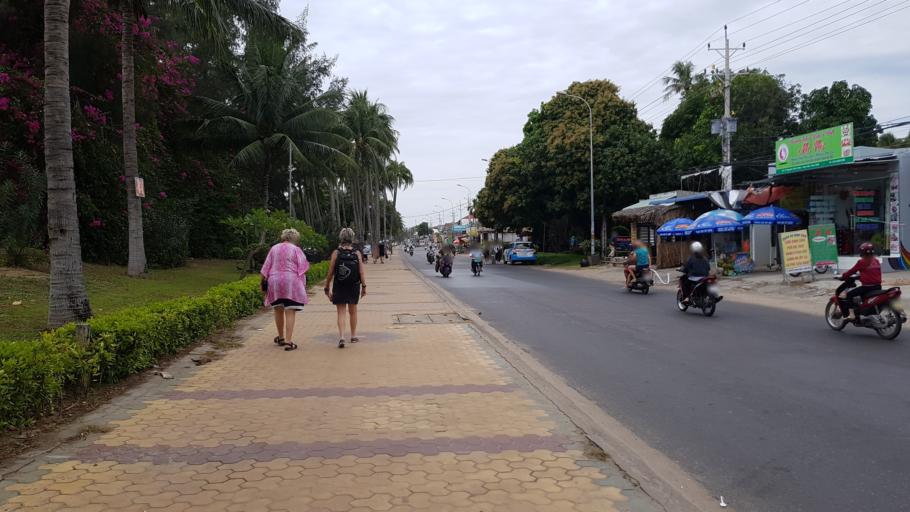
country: VN
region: Binh Thuan
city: Phan Thiet
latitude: 10.9486
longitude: 108.2046
